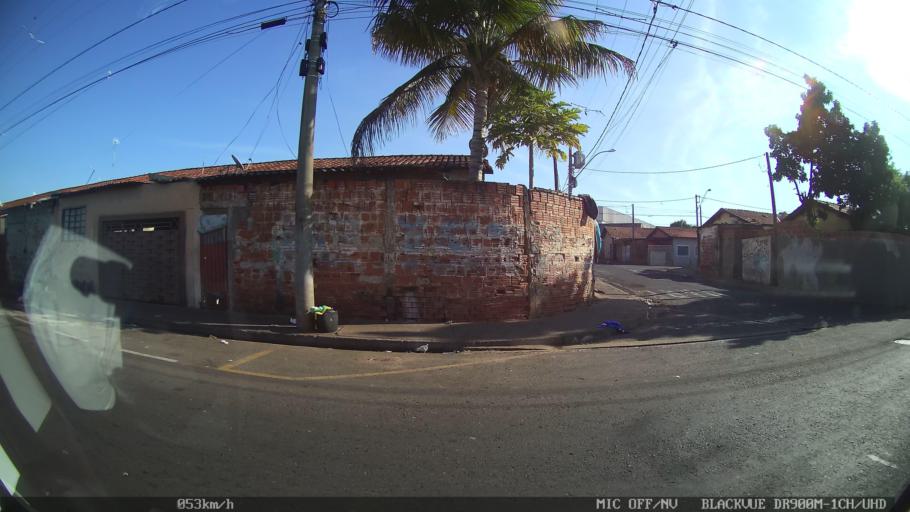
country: BR
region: Sao Paulo
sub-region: Sao Jose Do Rio Preto
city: Sao Jose do Rio Preto
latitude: -20.7664
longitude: -49.3835
